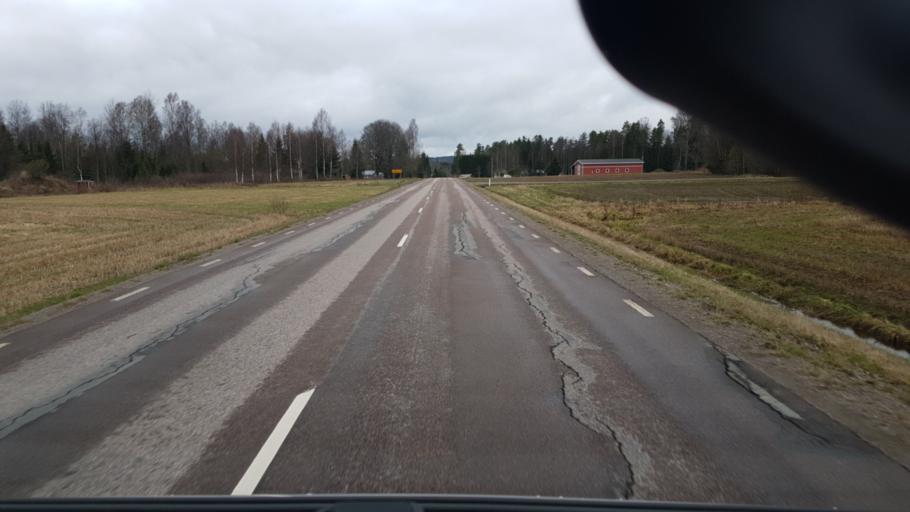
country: SE
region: Vaermland
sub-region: Eda Kommun
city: Charlottenberg
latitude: 59.9134
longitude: 12.2895
